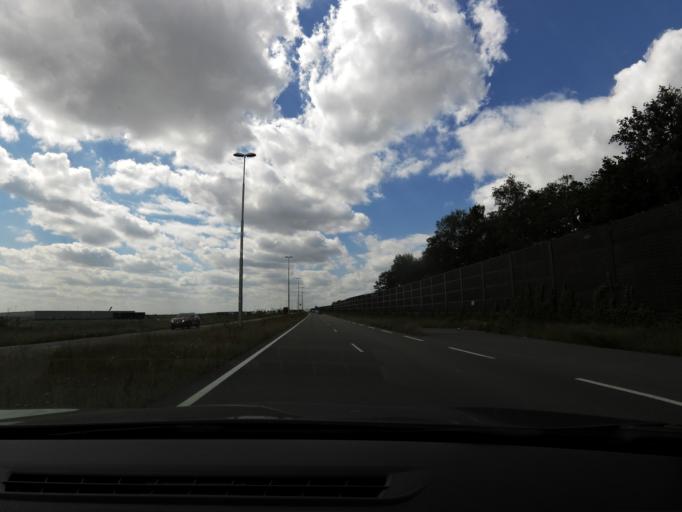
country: NL
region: North Brabant
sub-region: Gemeente Dongen
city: Dongen
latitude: 51.6076
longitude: 4.9911
